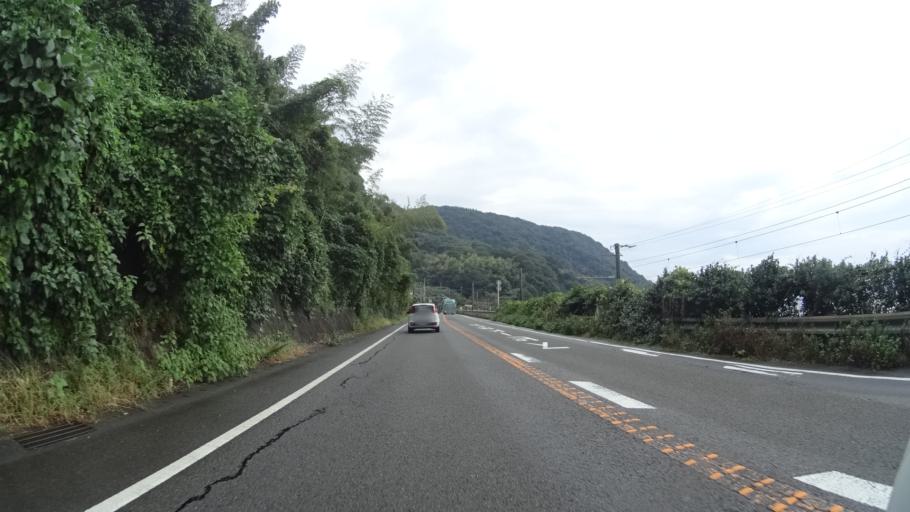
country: JP
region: Kagoshima
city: Kagoshima-shi
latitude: 31.6209
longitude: 130.5850
